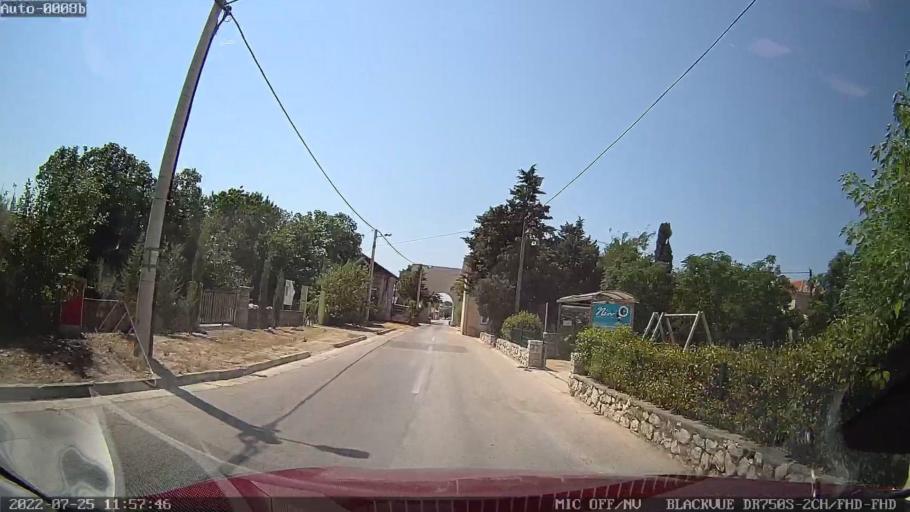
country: HR
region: Zadarska
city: Vrsi
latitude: 44.2412
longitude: 15.2131
